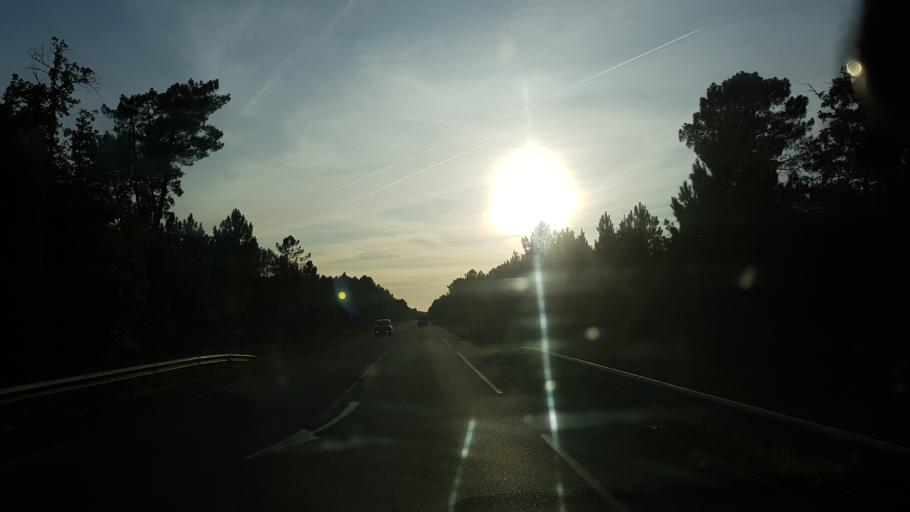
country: FR
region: Aquitaine
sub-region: Departement de la Gironde
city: Martignas-sur-Jalle
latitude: 44.8393
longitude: -0.7539
